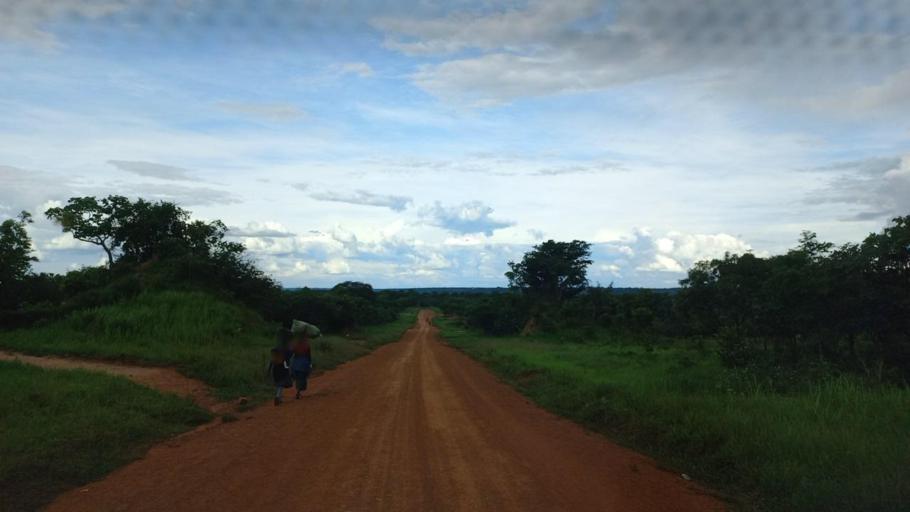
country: ZM
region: North-Western
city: Mwinilunga
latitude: -11.7618
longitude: 24.4160
